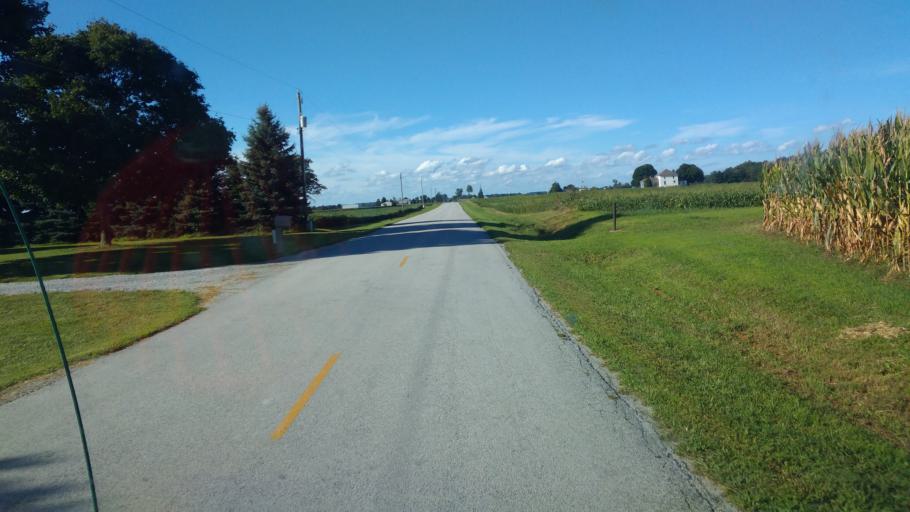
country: US
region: Ohio
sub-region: Hardin County
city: Kenton
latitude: 40.7522
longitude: -83.6905
